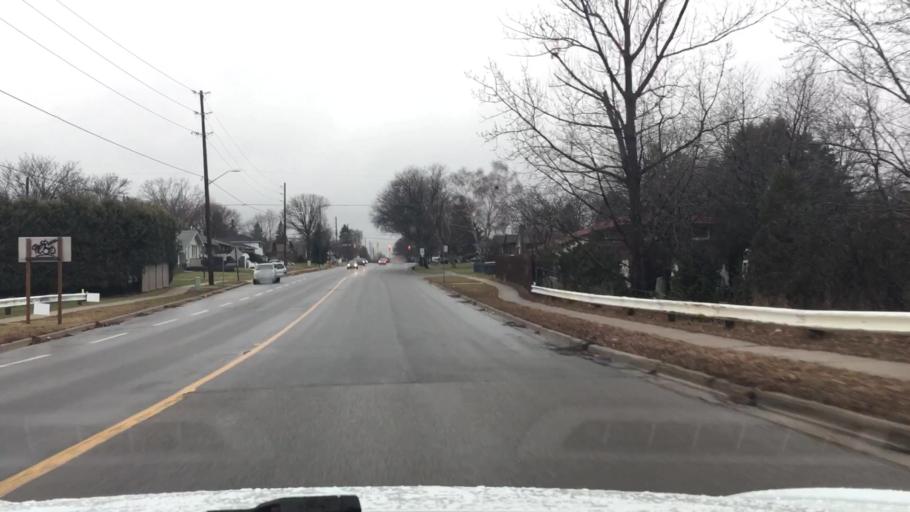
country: CA
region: Ontario
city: Oshawa
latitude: 43.8961
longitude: -78.8265
